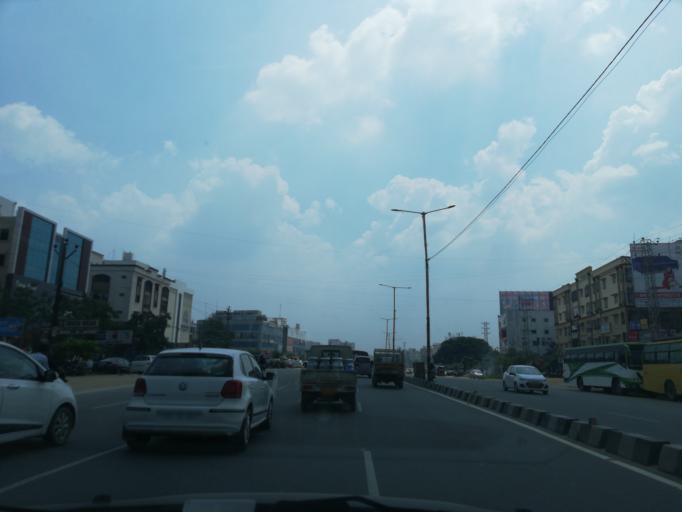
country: IN
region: Telangana
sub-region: Medak
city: Serilingampalle
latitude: 17.4956
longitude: 78.3363
